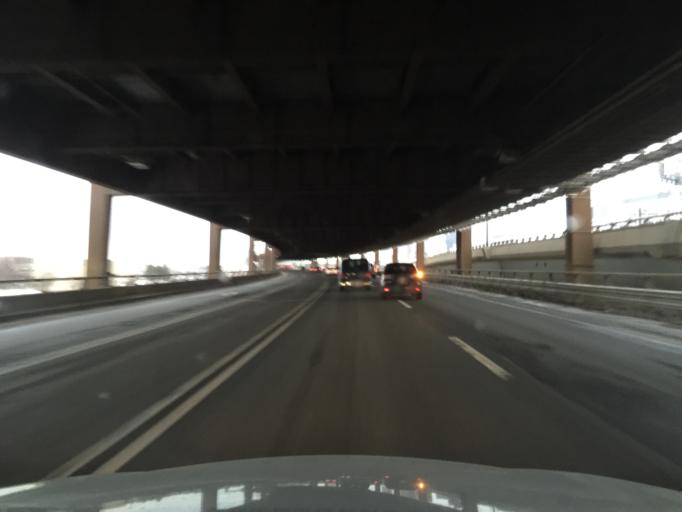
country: US
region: Massachusetts
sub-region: Suffolk County
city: Boston
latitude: 42.3757
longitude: -71.0735
